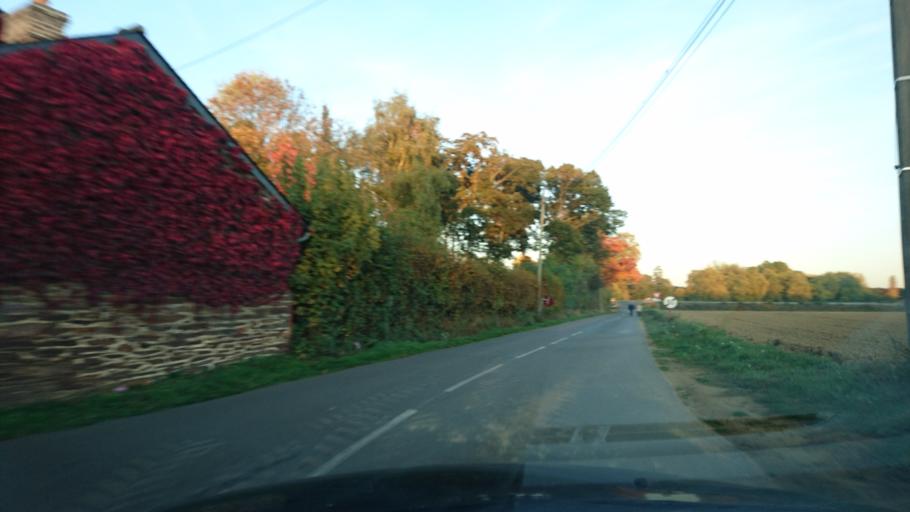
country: FR
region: Brittany
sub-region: Departement d'Ille-et-Vilaine
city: Bruz
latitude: 48.0132
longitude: -1.7482
